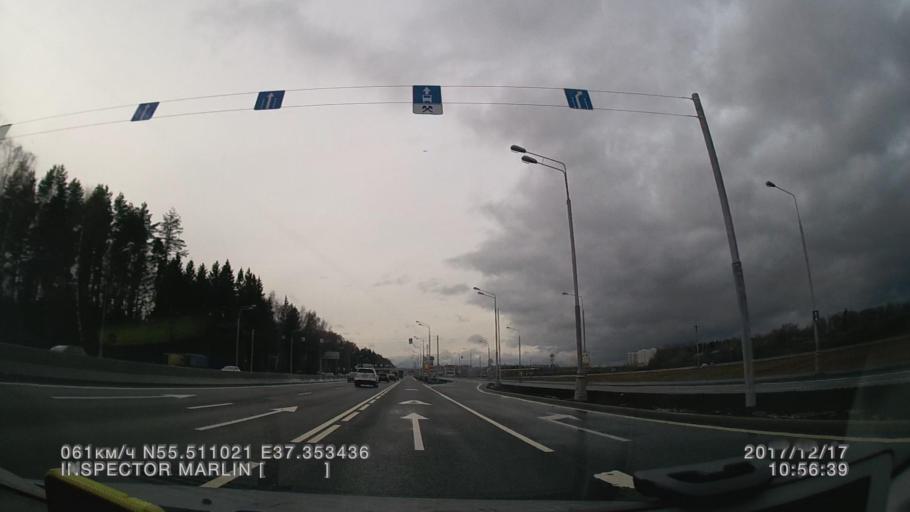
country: RU
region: Moskovskaya
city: Vatutinki
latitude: 55.5111
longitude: 37.3535
